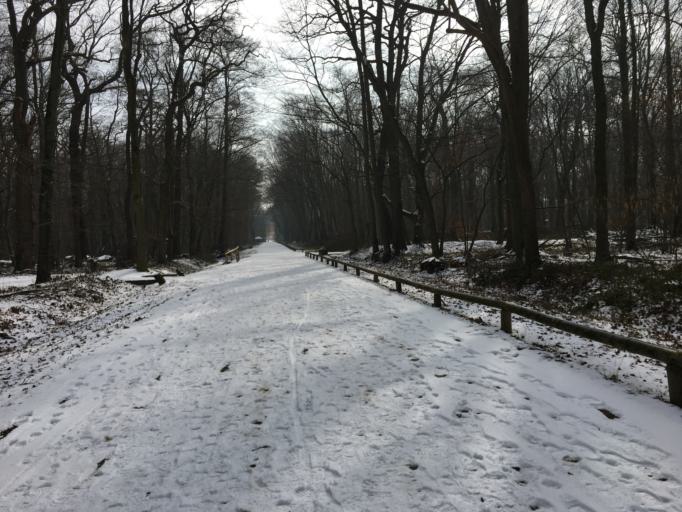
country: DE
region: North Rhine-Westphalia
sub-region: Regierungsbezirk Koln
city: Kreuzau
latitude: 50.7715
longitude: 6.5008
